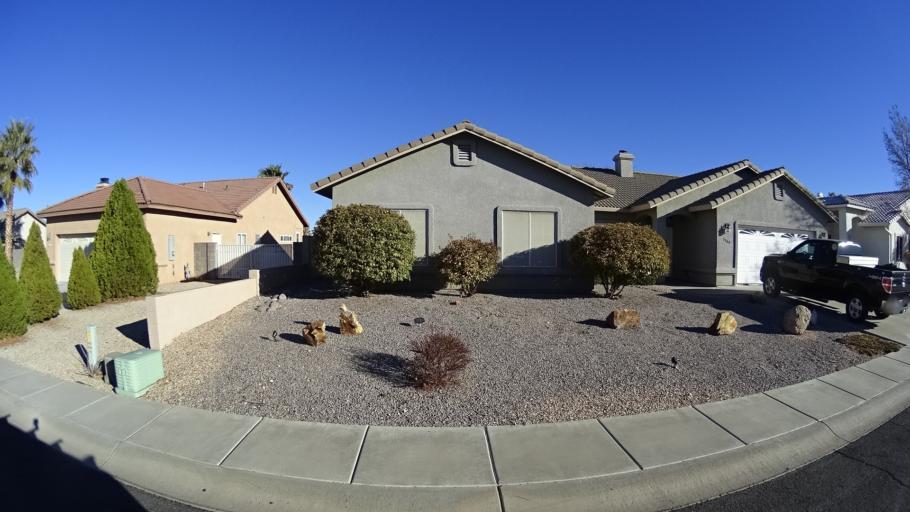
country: US
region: Arizona
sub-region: Mohave County
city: Kingman
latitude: 35.1926
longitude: -114.0047
